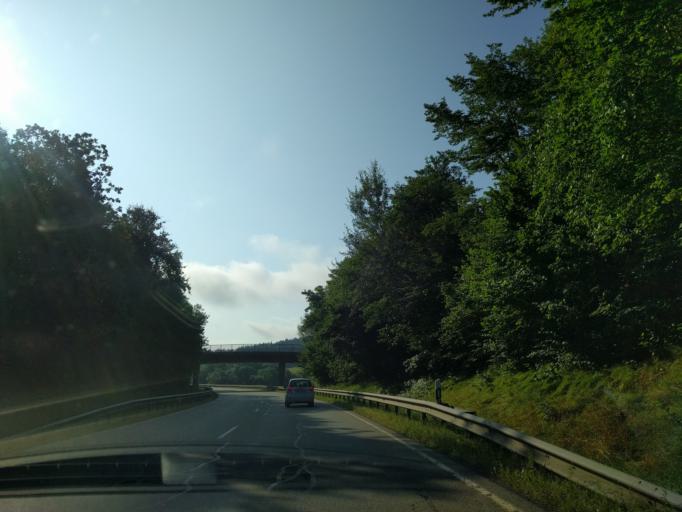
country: DE
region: Bavaria
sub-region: Lower Bavaria
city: Innernzell
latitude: 48.8341
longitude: 13.3162
